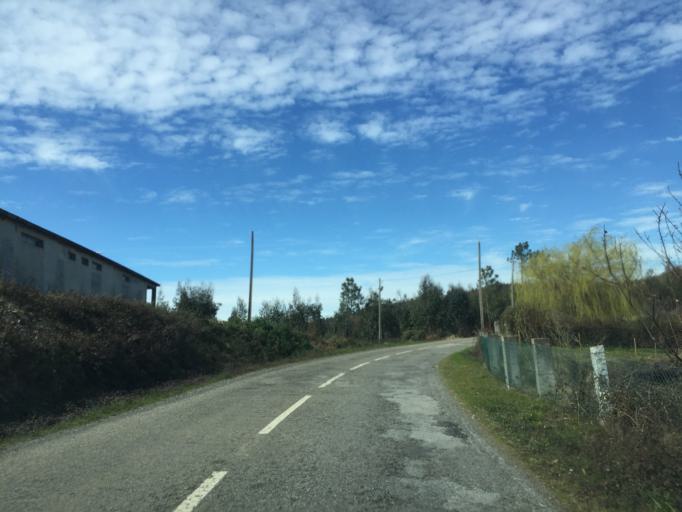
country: PT
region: Aveiro
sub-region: Arouca
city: Arouca
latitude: 40.9571
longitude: -8.2297
